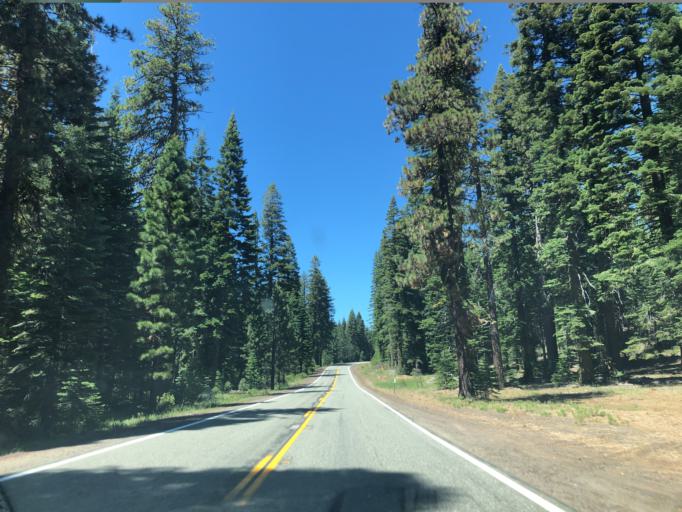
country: US
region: California
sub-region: Shasta County
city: Shingletown
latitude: 40.5491
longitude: -121.5790
